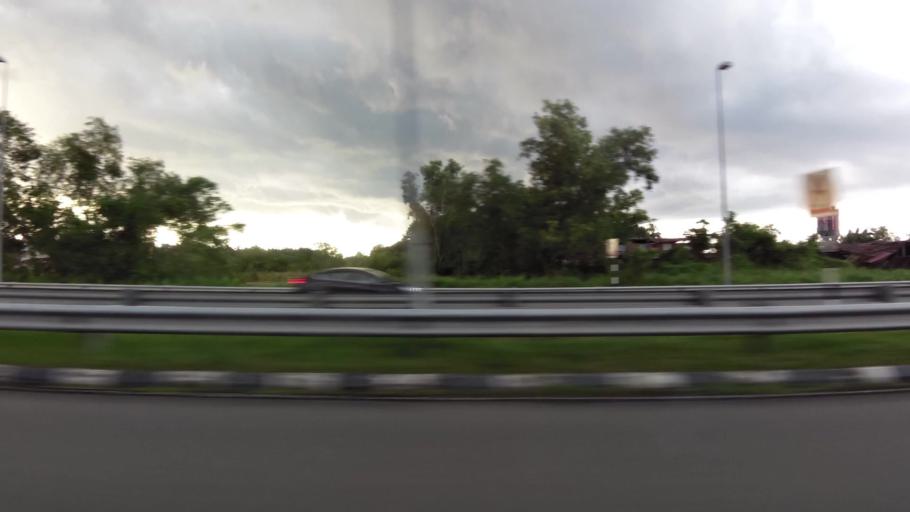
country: BN
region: Brunei and Muara
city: Bandar Seri Begawan
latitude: 4.9309
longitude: 114.9734
